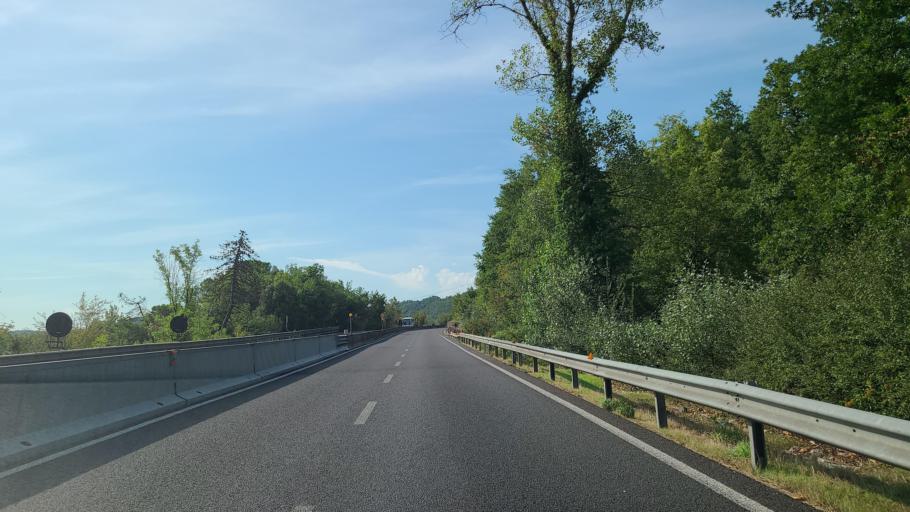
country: IT
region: Tuscany
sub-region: Province of Florence
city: San Casciano in Val di Pesa
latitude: 43.6731
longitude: 11.2102
